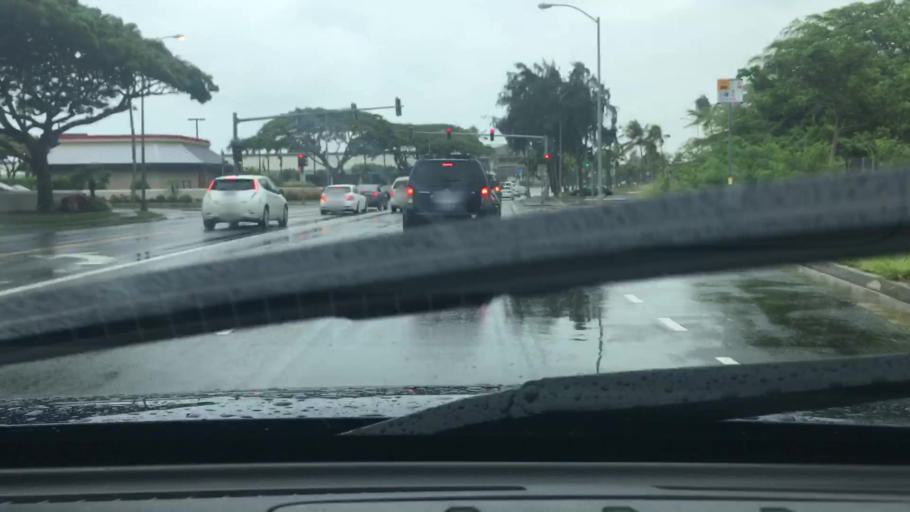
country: US
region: Hawaii
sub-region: Honolulu County
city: Waimanalo Beach
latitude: 21.2846
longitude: -157.7108
